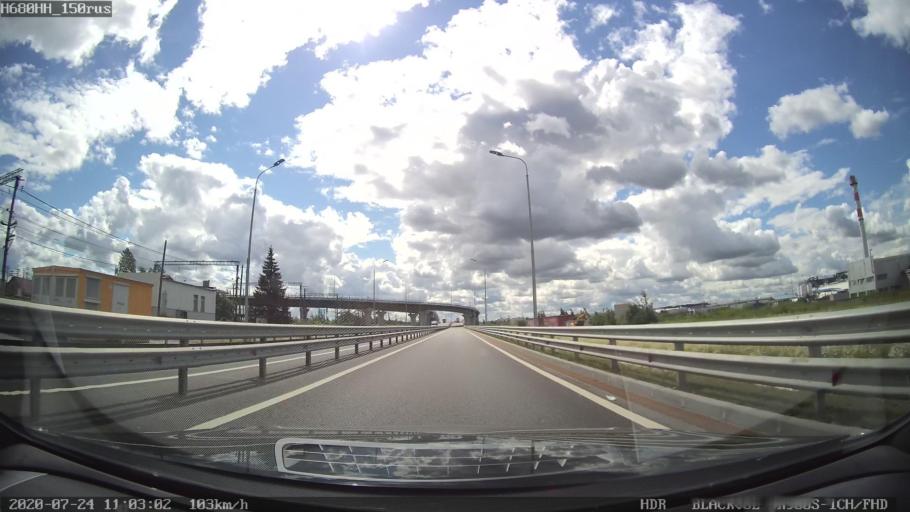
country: RU
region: St.-Petersburg
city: Shushary
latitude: 59.8083
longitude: 30.3314
